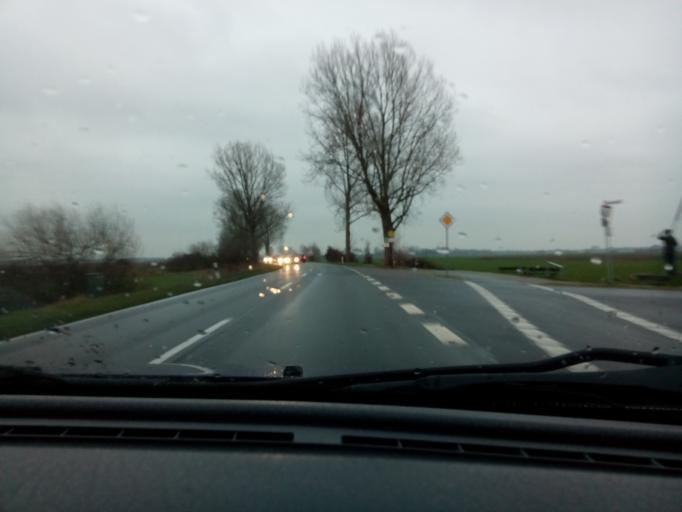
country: DE
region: Lower Saxony
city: Osterholz-Scharmbeck
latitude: 53.2174
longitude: 8.8087
